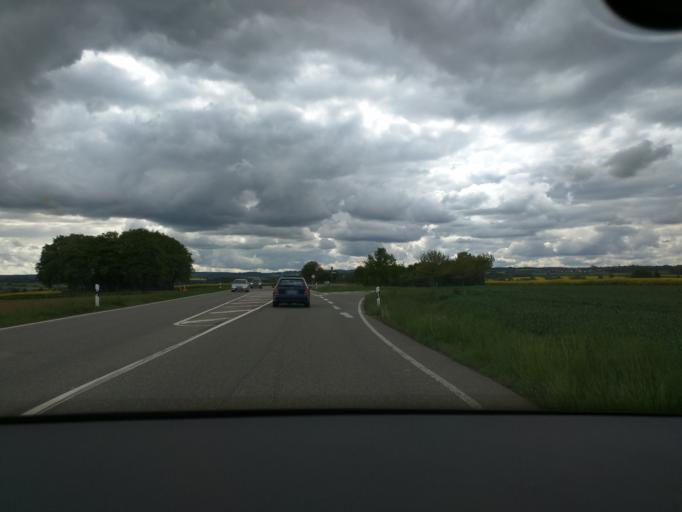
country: DE
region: Baden-Wuerttemberg
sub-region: Regierungsbezirk Stuttgart
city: Motzingen
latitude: 48.4831
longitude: 8.7762
